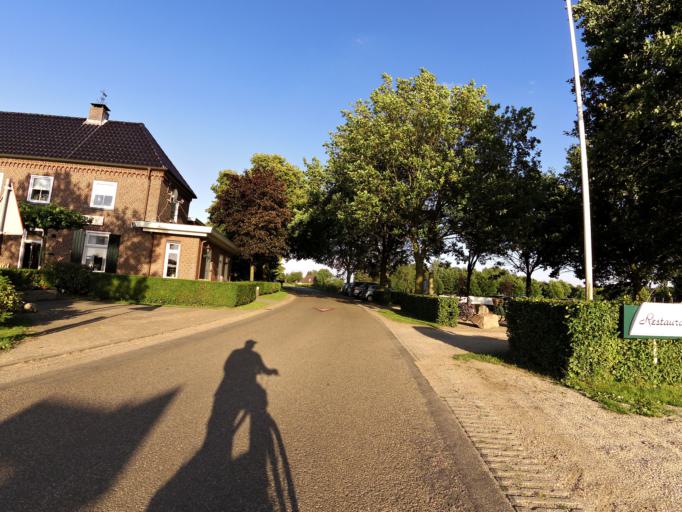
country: NL
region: Gelderland
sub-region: Oude IJsselstreek
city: Gendringen
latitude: 51.8720
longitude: 6.4164
